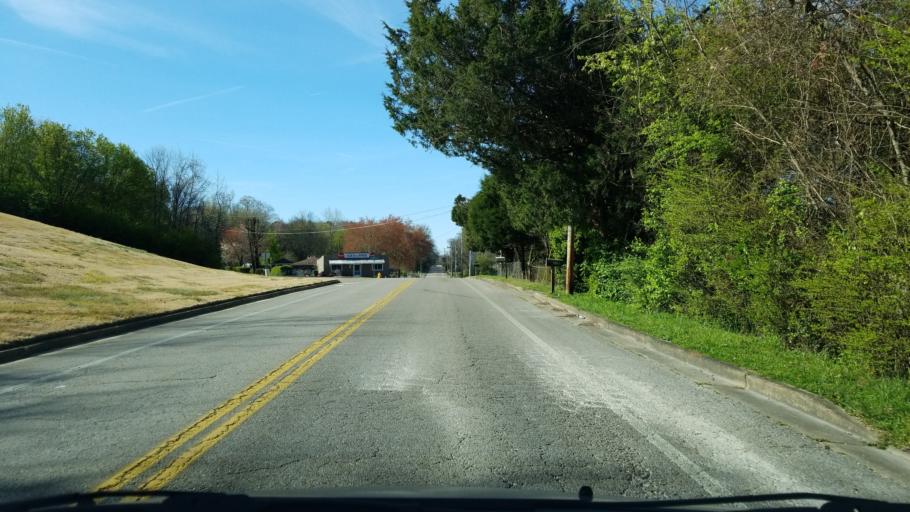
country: US
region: Tennessee
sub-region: Hamilton County
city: East Brainerd
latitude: 35.0497
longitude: -85.1813
